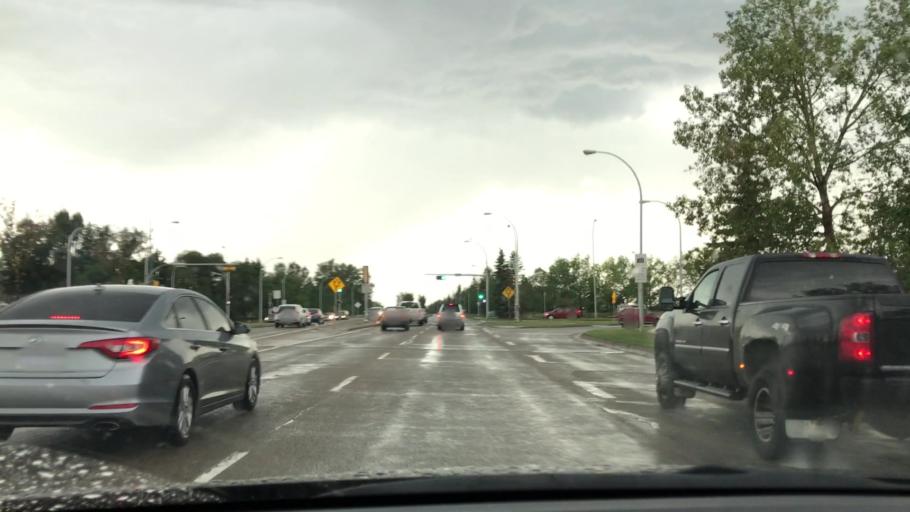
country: CA
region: Alberta
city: Edmonton
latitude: 53.4536
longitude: -113.4332
